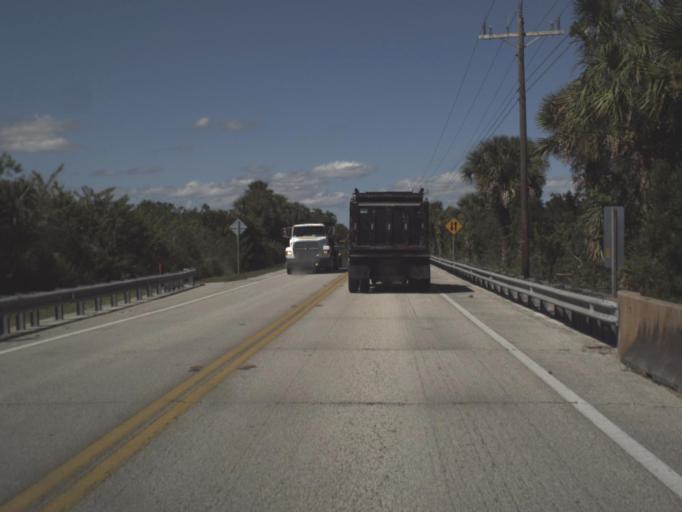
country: US
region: Florida
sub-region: Collier County
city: Marco
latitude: 25.9609
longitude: -81.5164
